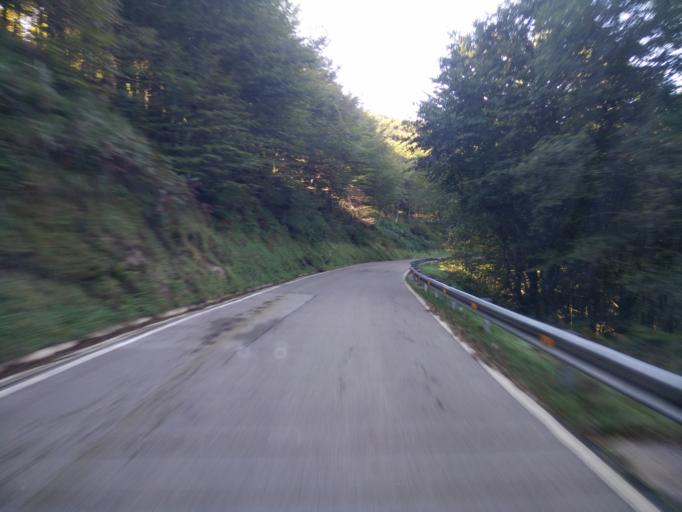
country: ES
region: Cantabria
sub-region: Provincia de Cantabria
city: San Pedro del Romeral
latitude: 43.0532
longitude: -3.8424
